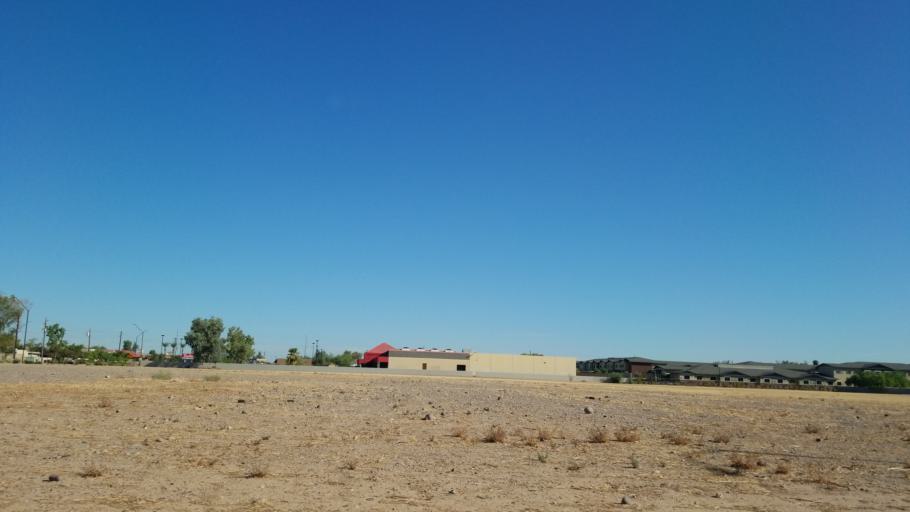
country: US
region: Arizona
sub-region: Maricopa County
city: Avondale
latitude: 33.4463
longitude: -112.3489
